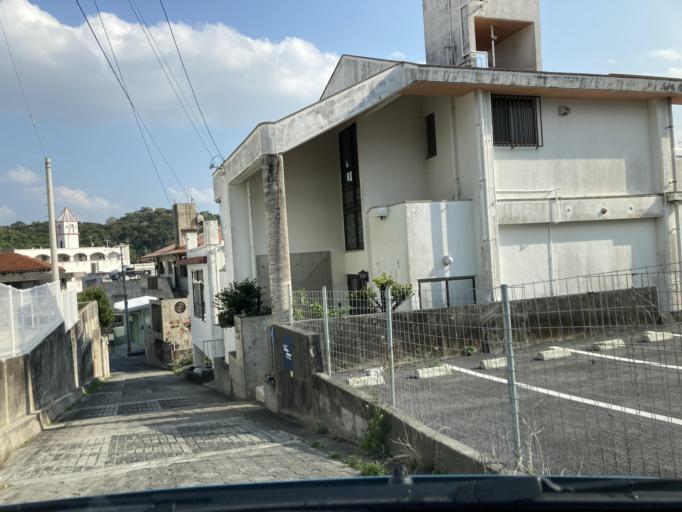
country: JP
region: Okinawa
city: Tomigusuku
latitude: 26.1889
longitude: 127.7275
